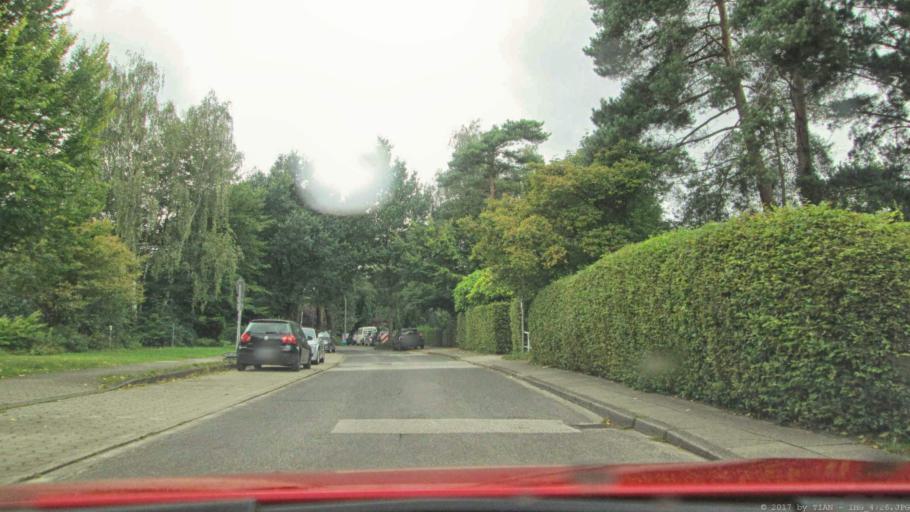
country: DE
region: Hamburg
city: Eidelstedt
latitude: 53.5640
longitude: 9.8537
